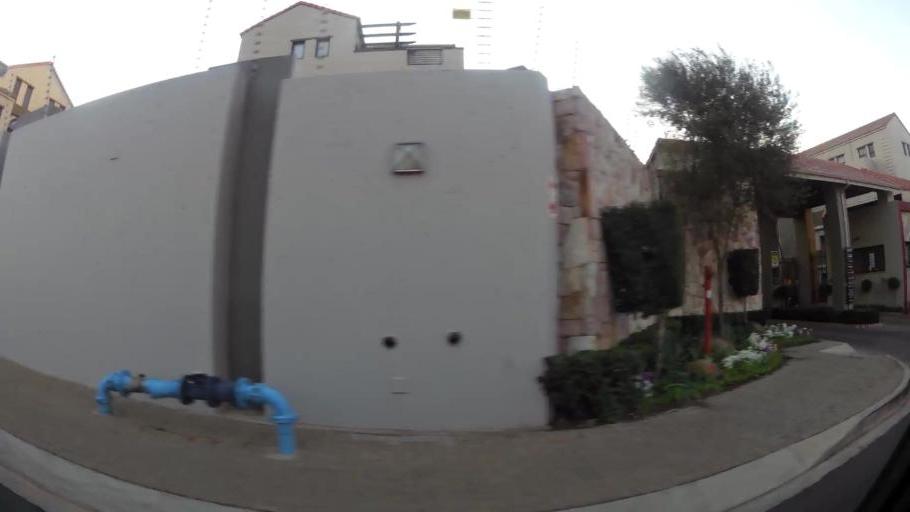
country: ZA
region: Gauteng
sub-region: City of Johannesburg Metropolitan Municipality
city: Diepsloot
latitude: -26.0139
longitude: 28.0373
